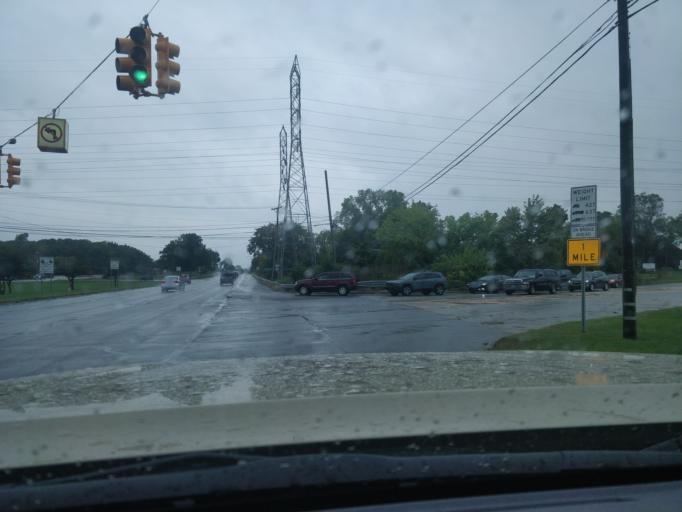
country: US
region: Michigan
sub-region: Wayne County
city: Trenton
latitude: 42.1271
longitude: -83.2024
